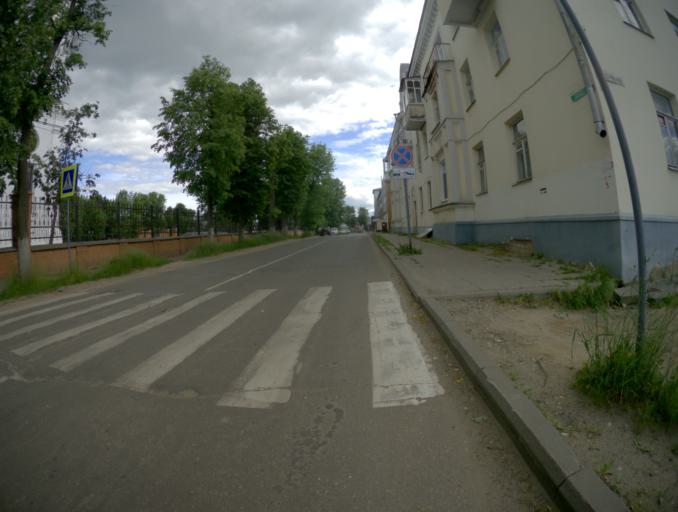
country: RU
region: Ivanovo
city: Shuya
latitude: 56.8568
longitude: 41.3831
